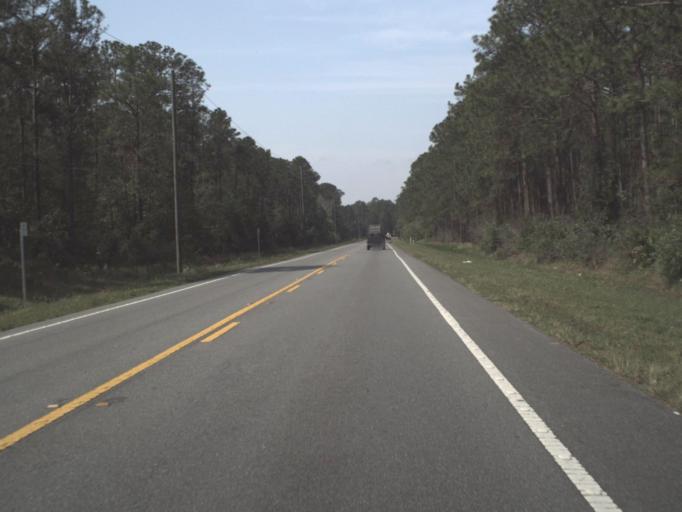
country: US
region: Florida
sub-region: Lake County
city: Astor
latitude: 29.1604
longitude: -81.5537
